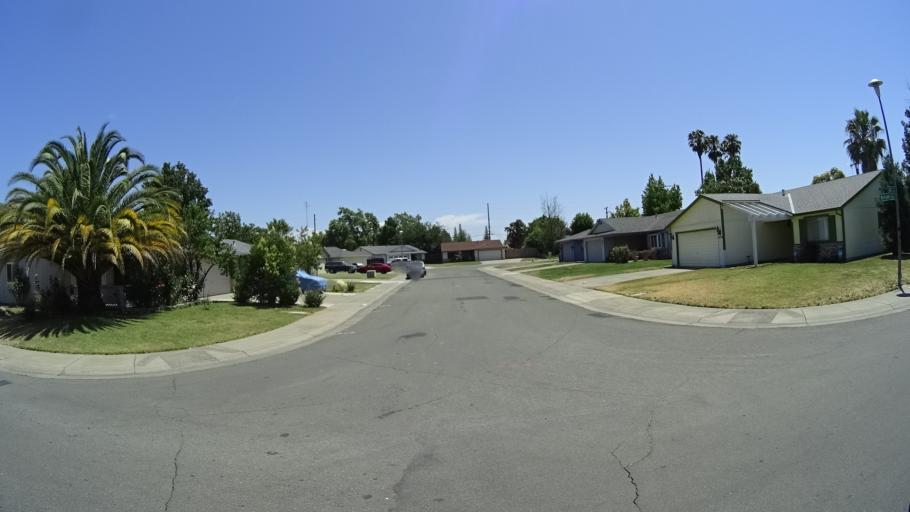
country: US
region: California
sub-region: Sacramento County
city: Florin
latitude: 38.5285
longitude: -121.4312
